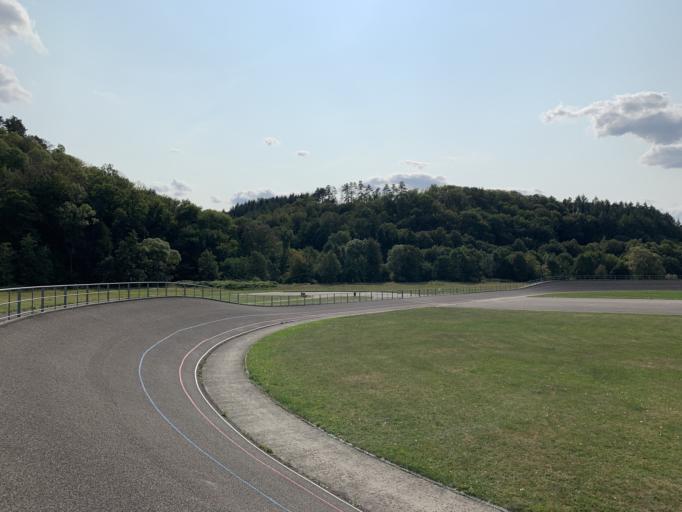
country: BE
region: Wallonia
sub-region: Province de Namur
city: Rochefort
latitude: 50.1576
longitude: 5.2417
